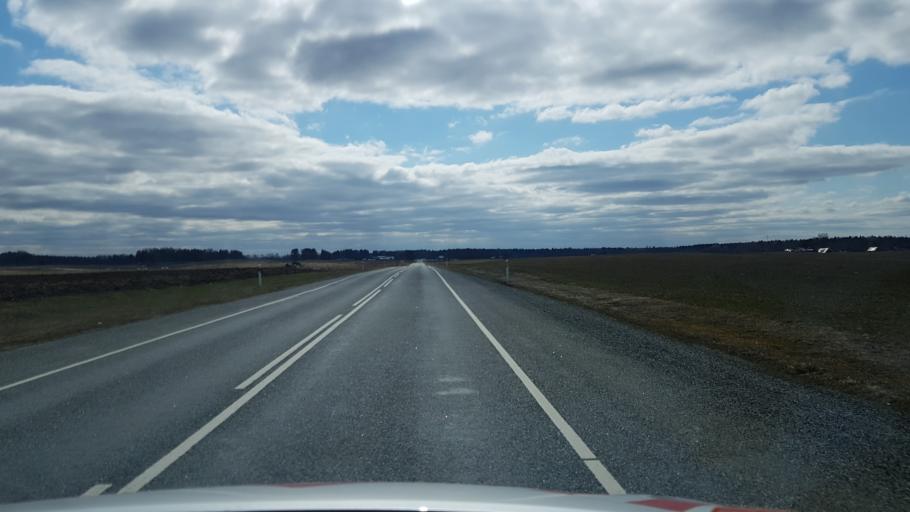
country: EE
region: Laeaene-Virumaa
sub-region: Tapa vald
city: Tapa
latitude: 59.3030
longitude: 25.9997
